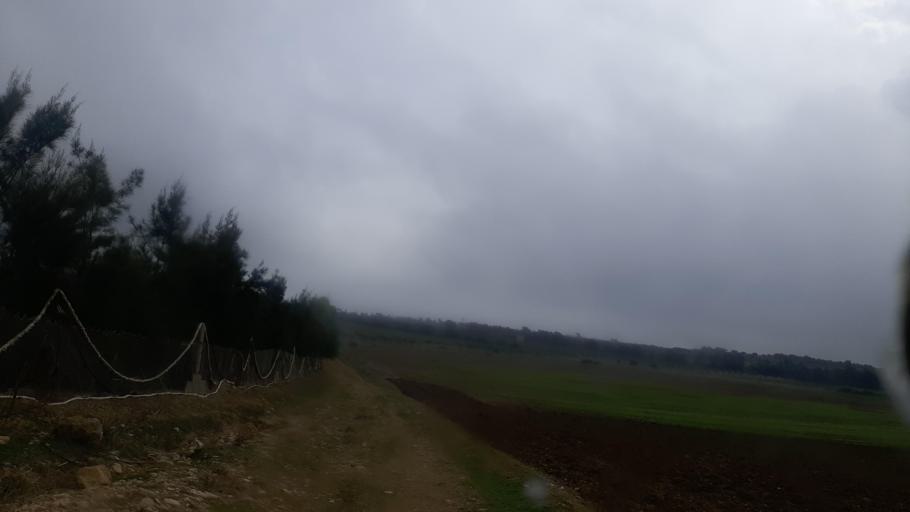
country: TN
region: Nabul
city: Qulaybiyah
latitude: 36.8268
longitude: 11.0358
